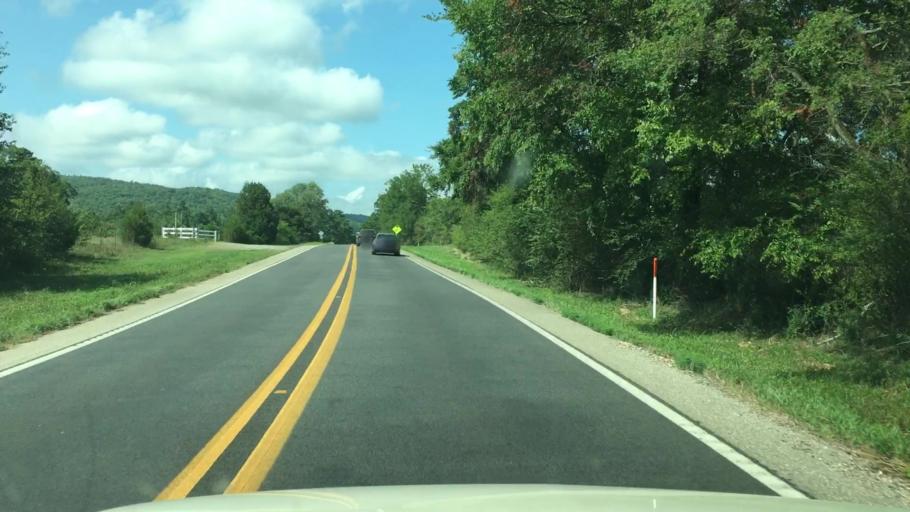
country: US
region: Arkansas
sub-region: Garland County
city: Lake Hamilton
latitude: 34.3951
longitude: -93.1112
